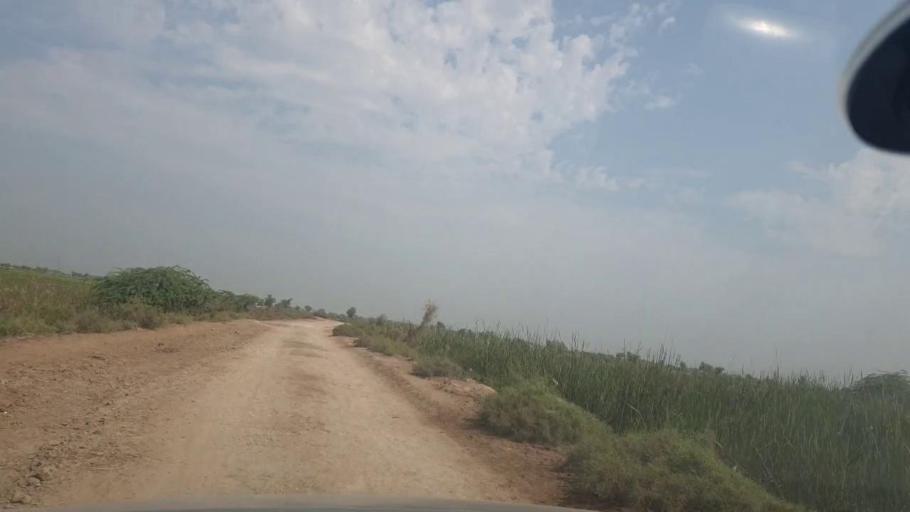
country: PK
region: Balochistan
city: Mehrabpur
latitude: 28.1186
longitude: 68.0912
